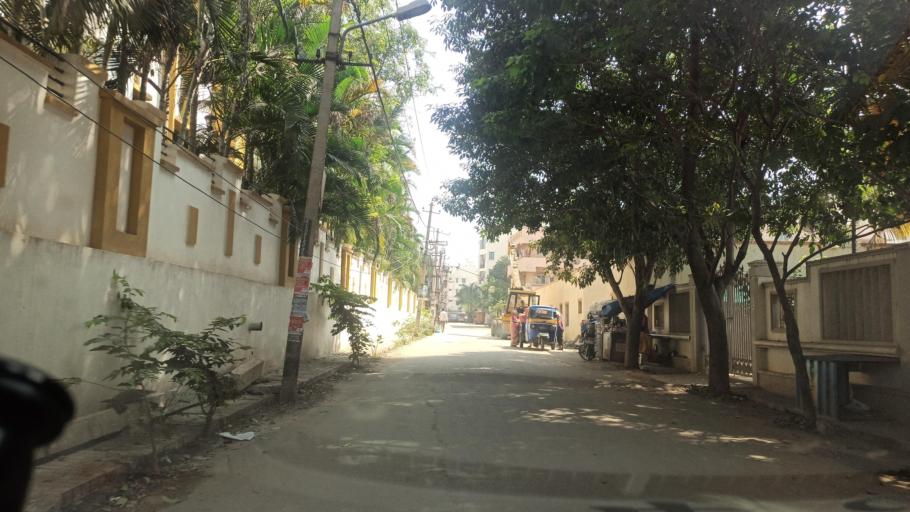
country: IN
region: Karnataka
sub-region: Bangalore Urban
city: Bangalore
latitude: 12.9528
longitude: 77.6965
